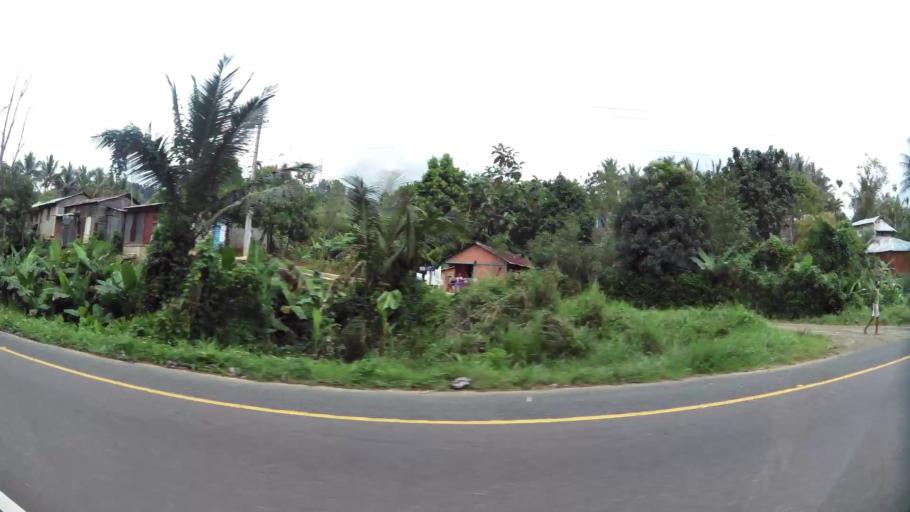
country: DO
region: Monsenor Nouel
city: Piedra Blanca
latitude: 18.7964
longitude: -70.2731
